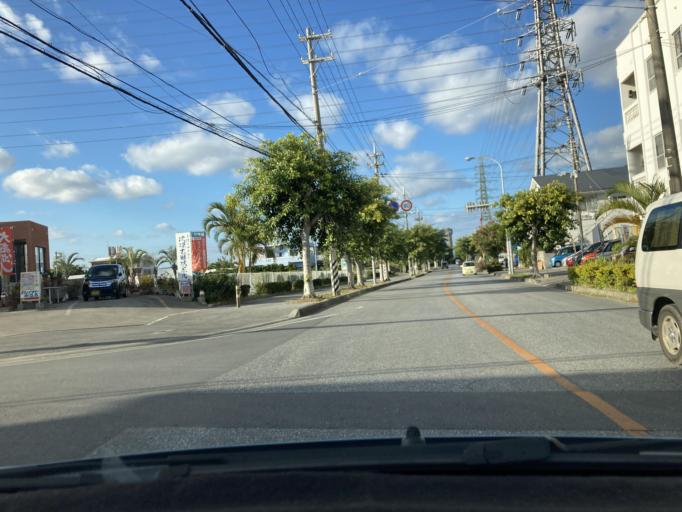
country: JP
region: Okinawa
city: Gushikawa
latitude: 26.3559
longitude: 127.8638
